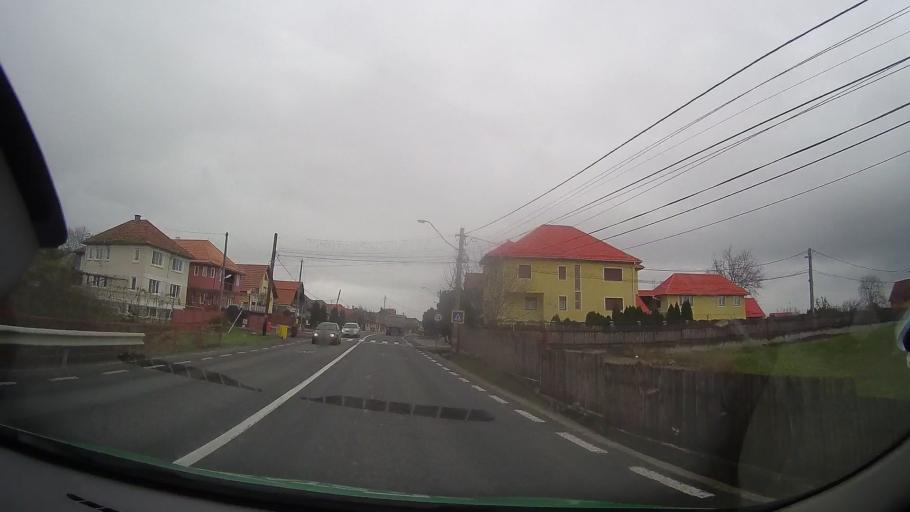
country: RO
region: Mures
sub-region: Municipiul Reghin
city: Reghin
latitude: 46.7706
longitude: 24.6862
